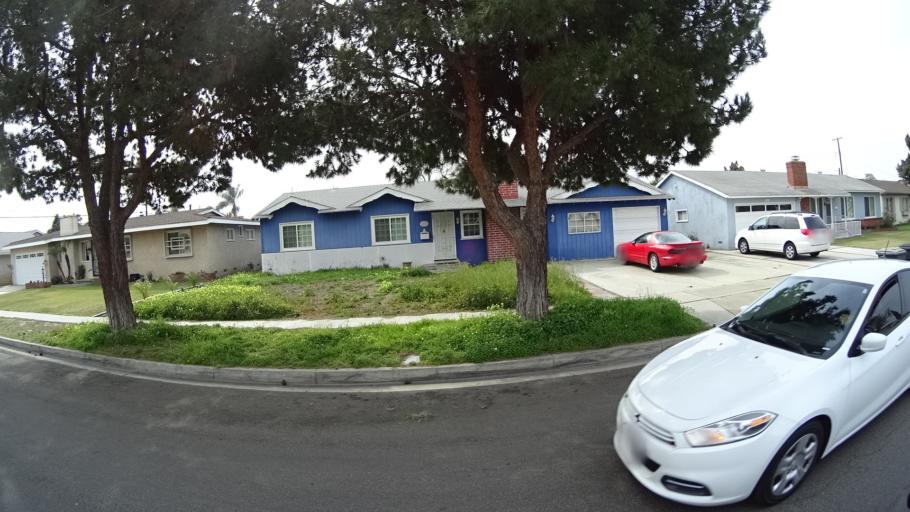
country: US
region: California
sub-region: Orange County
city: Stanton
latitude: 33.8064
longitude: -117.9619
